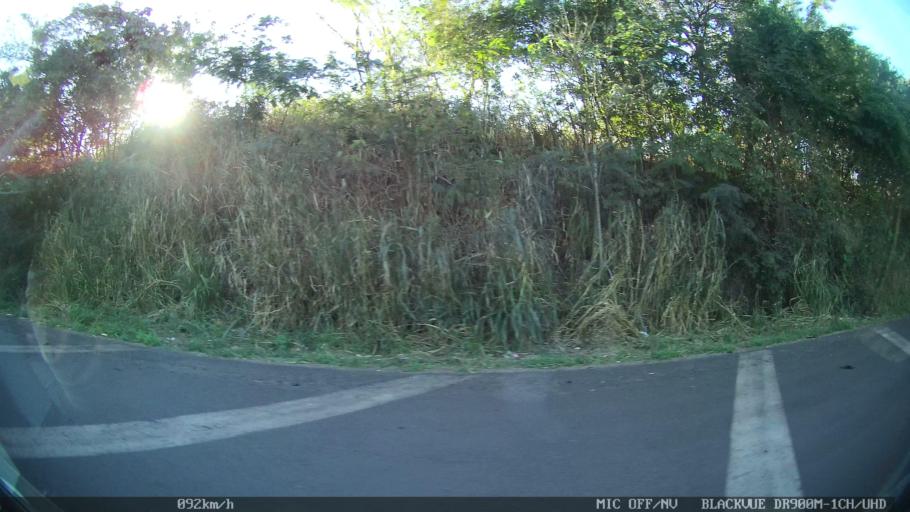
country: BR
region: Sao Paulo
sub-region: Guapiacu
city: Guapiacu
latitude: -20.7569
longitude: -49.1612
